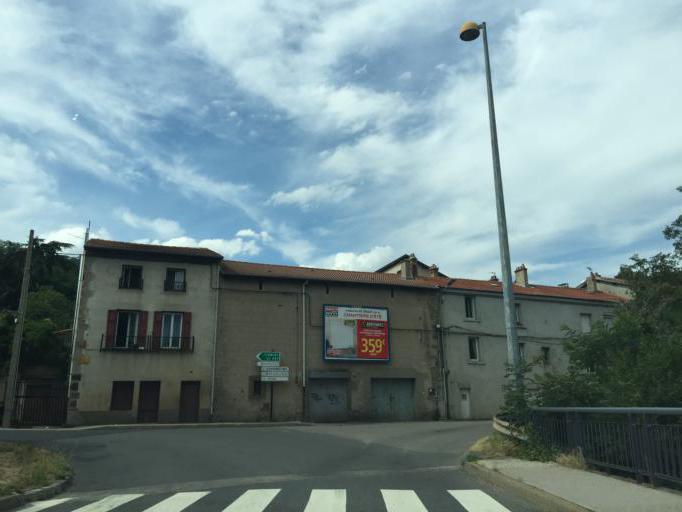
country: FR
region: Rhone-Alpes
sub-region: Departement de la Loire
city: Saint-Jean-Bonnefonds
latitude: 45.4350
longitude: 4.4311
